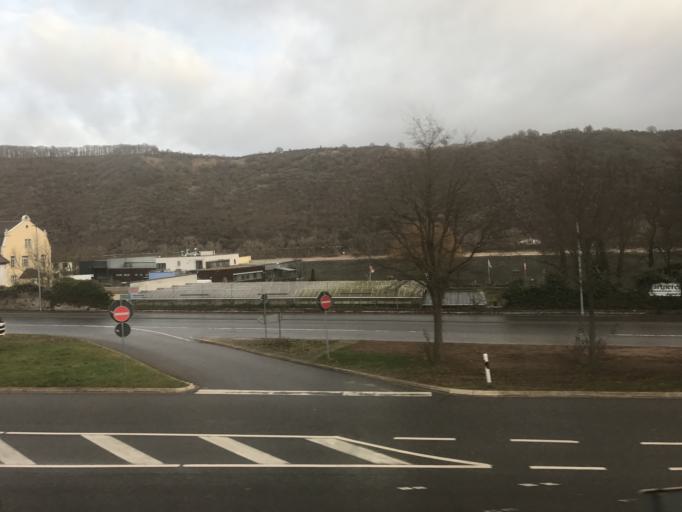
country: DE
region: Rheinland-Pfalz
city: Boppard
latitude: 50.2289
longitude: 7.6048
